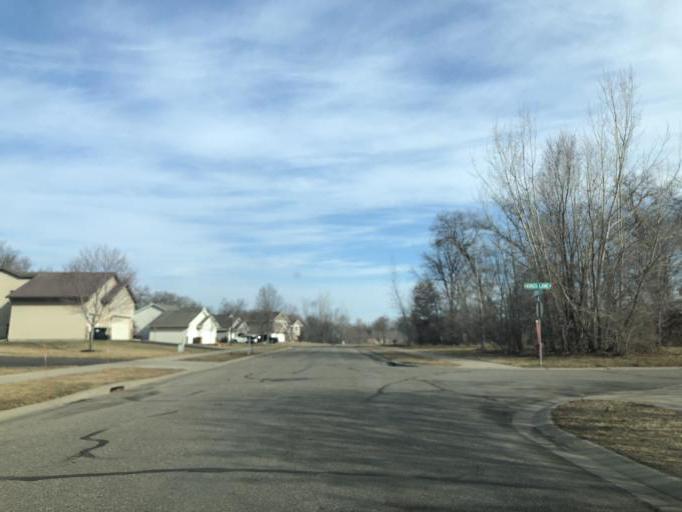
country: US
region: Minnesota
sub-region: Sherburne County
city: Becker
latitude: 45.4003
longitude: -93.8535
